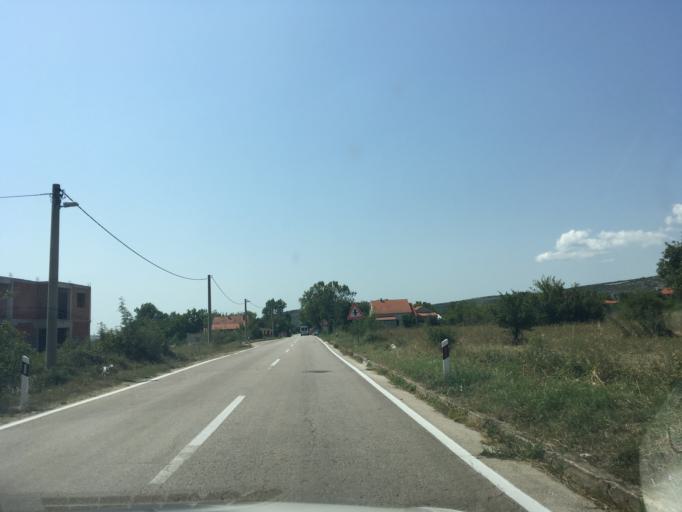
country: HR
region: Sibensko-Kniniska
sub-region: Grad Sibenik
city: Pirovac
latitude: 43.9607
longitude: 15.7683
